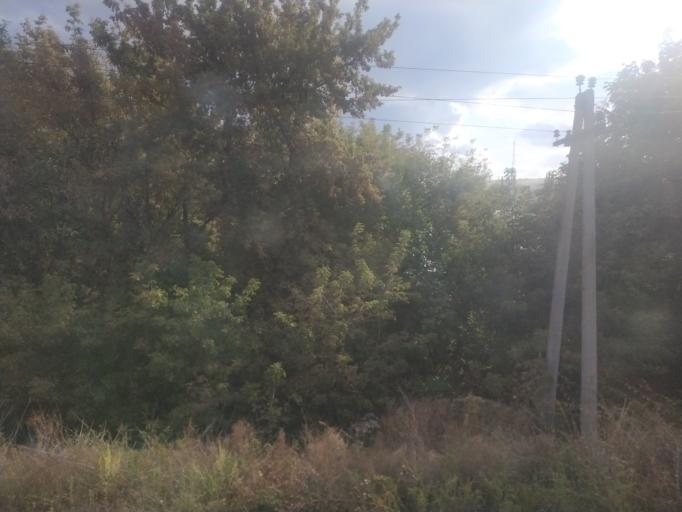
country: RU
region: Volgograd
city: Krasnoslobodsk
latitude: 48.5077
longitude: 44.5426
